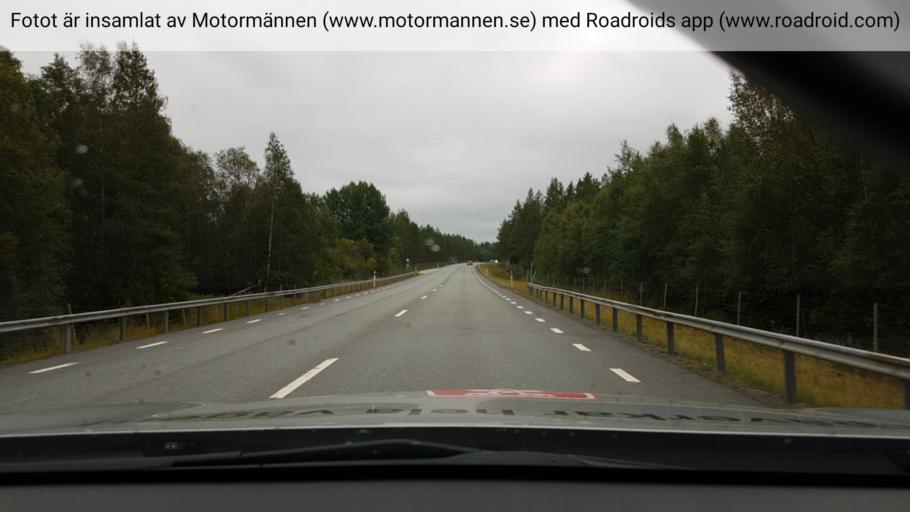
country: SE
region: Vaesterbotten
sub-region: Robertsfors Kommun
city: Robertsfors
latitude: 64.0485
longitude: 20.8487
